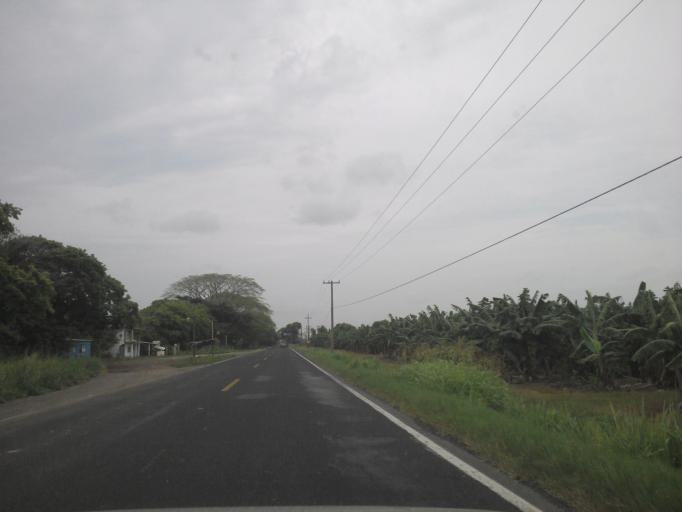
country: MX
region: Veracruz
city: Nautla
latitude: 20.2211
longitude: -96.7861
